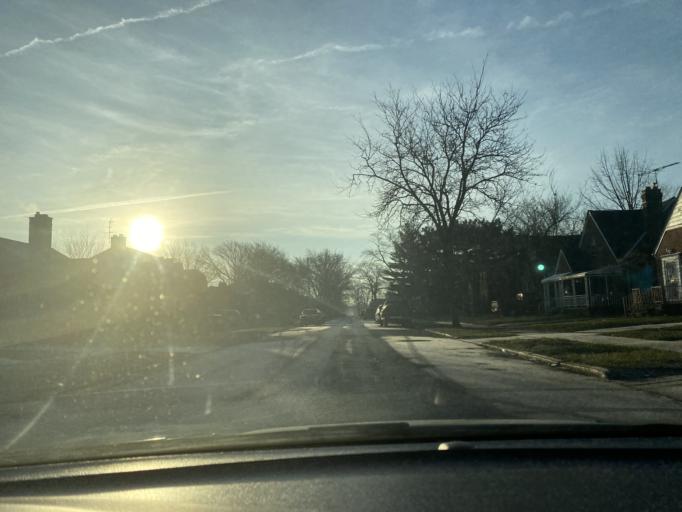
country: US
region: Michigan
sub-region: Wayne County
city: Grosse Pointe Park
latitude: 42.4058
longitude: -82.9458
